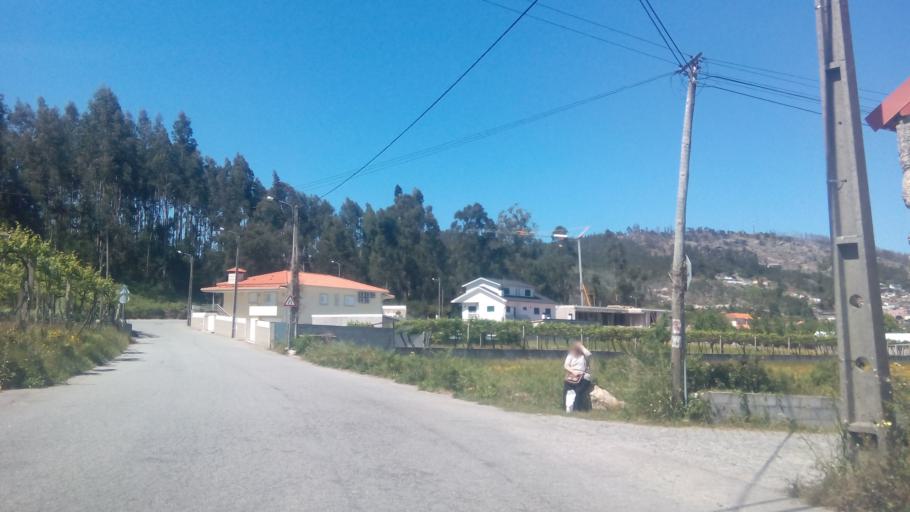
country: PT
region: Porto
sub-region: Paredes
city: Baltar
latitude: 41.1848
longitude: -8.3941
